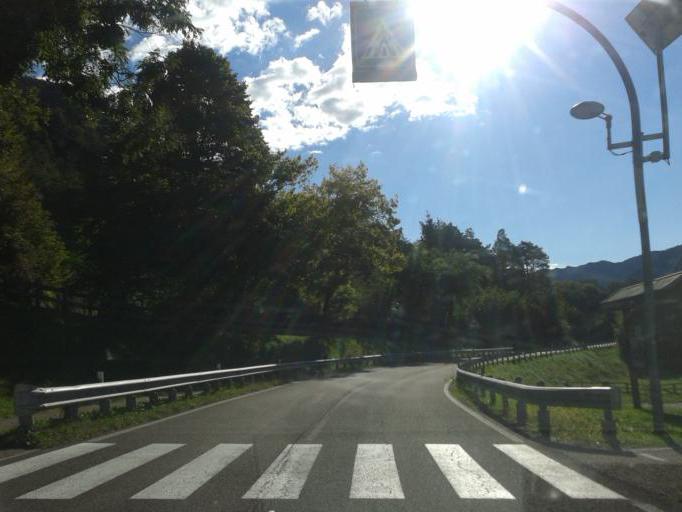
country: IT
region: Trentino-Alto Adige
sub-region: Provincia di Trento
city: Molina di Ledro
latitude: 45.8802
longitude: 10.7602
